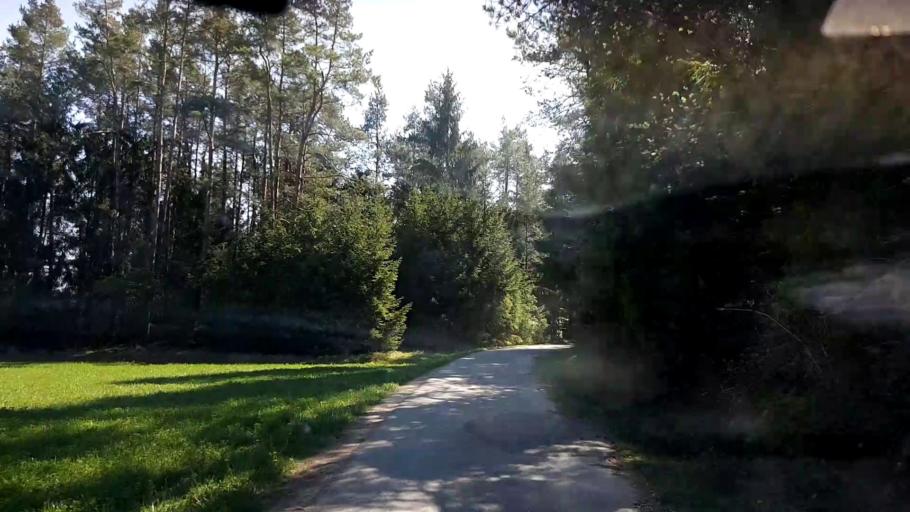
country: DE
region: Bavaria
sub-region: Upper Franconia
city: Konigsfeld
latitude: 49.9068
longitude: 11.1748
